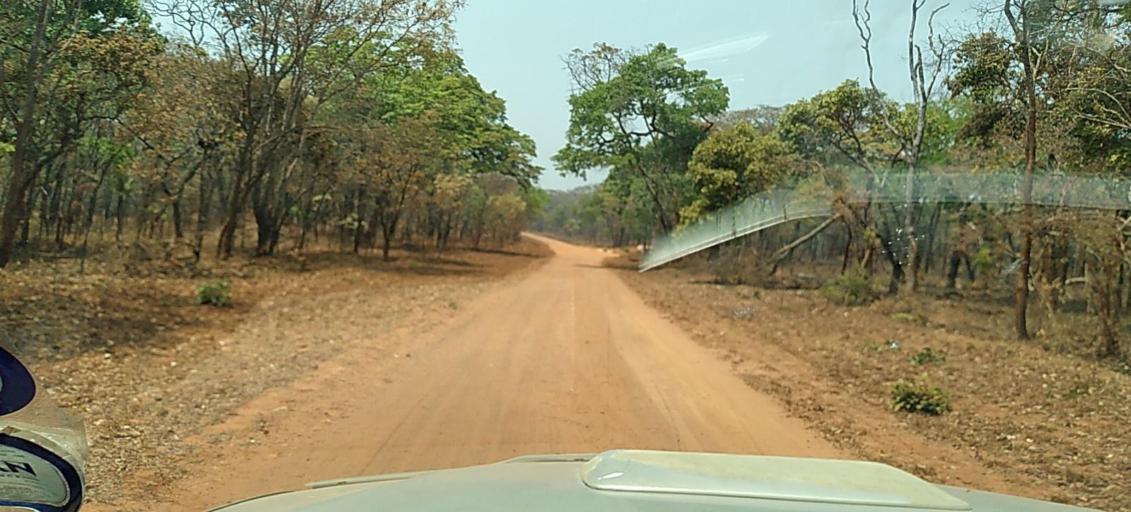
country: ZM
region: North-Western
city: Kasempa
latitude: -13.5614
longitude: 26.0837
